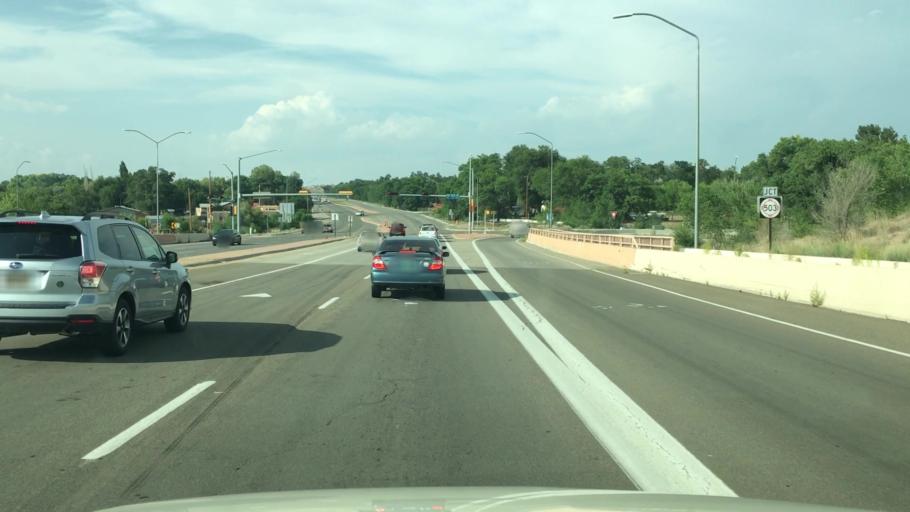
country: US
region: New Mexico
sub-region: Santa Fe County
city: Pojoaque
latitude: 35.8962
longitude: -106.0216
